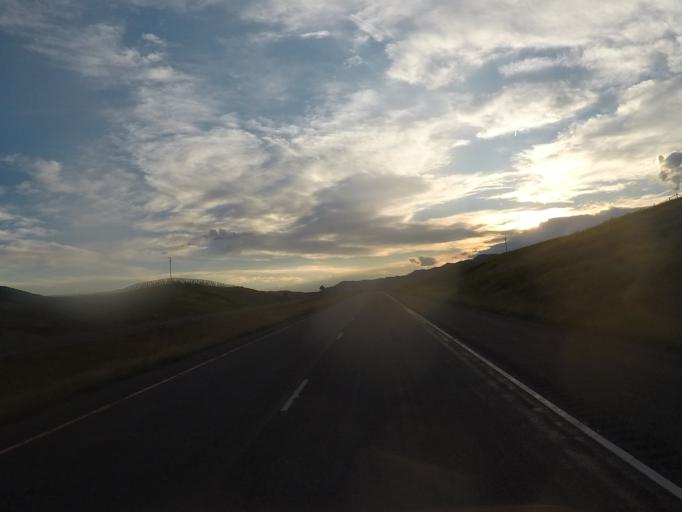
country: US
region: Montana
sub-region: Park County
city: Livingston
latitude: 45.6462
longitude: -110.5909
